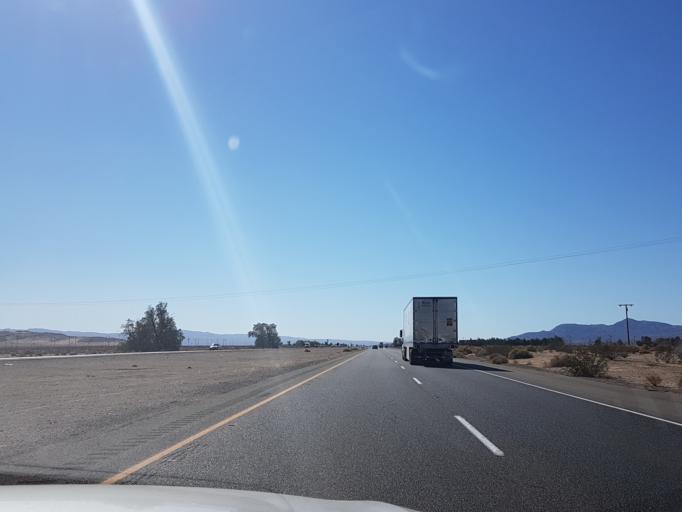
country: US
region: California
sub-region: San Bernardino County
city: Fort Irwin
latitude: 34.9605
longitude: -116.6523
